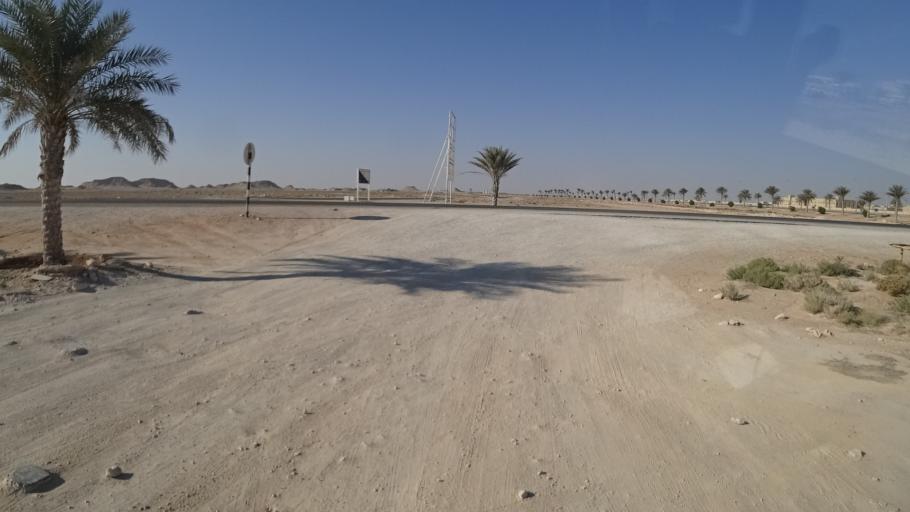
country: OM
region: Zufar
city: Salalah
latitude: 17.6118
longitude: 54.0313
